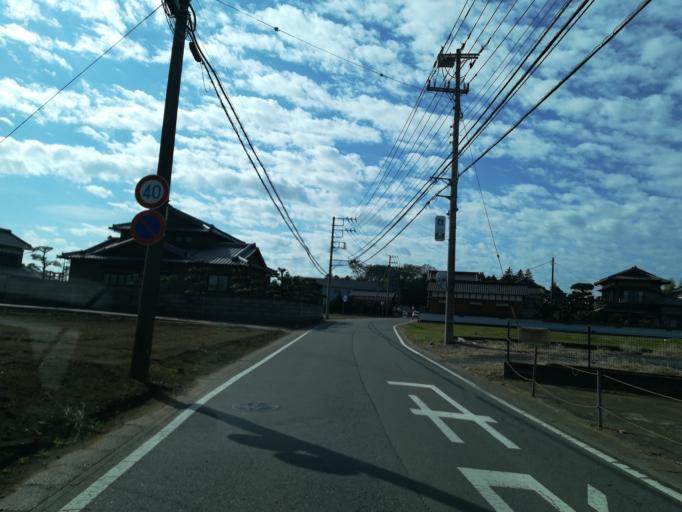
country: JP
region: Ibaraki
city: Naka
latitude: 36.0759
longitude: 140.0943
